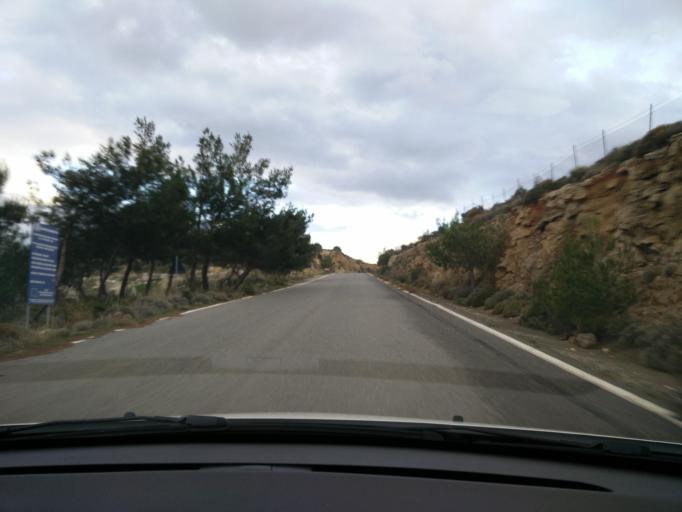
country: GR
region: Crete
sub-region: Nomos Lasithiou
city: Gra Liyia
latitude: 35.0882
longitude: 25.7032
